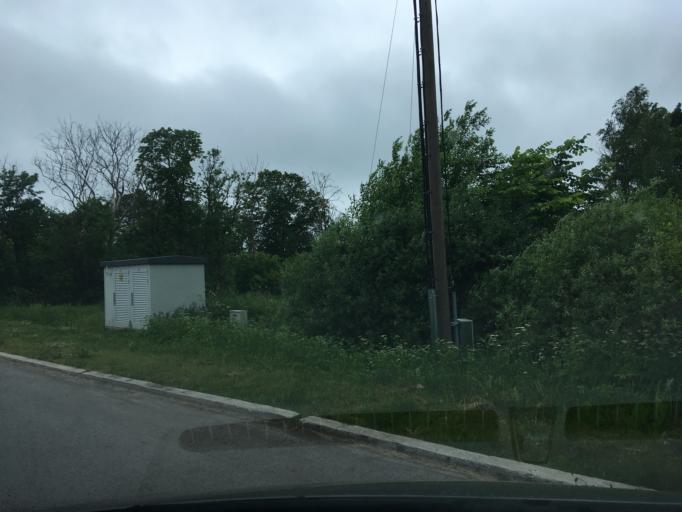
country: EE
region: Laeaene
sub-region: Lihula vald
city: Lihula
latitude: 58.6890
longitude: 23.8337
